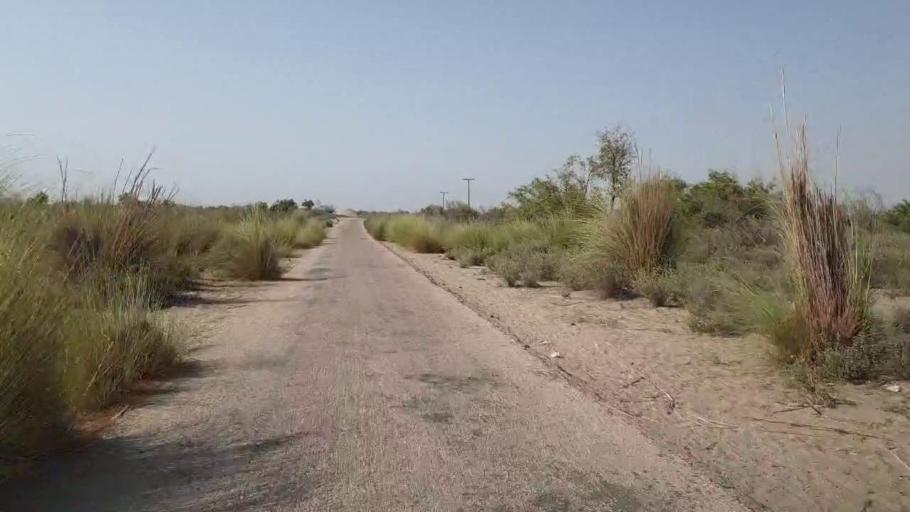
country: PK
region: Sindh
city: Jam Sahib
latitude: 26.5832
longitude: 68.9210
